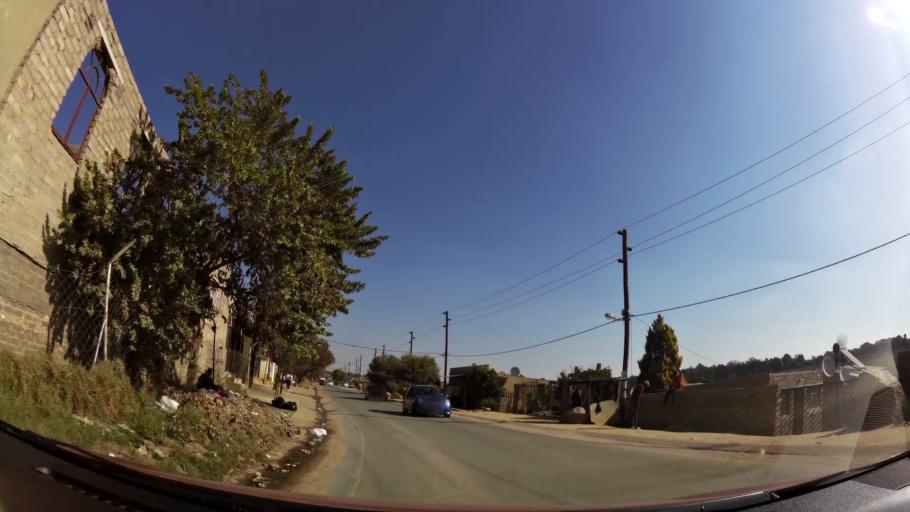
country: ZA
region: Gauteng
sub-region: West Rand District Municipality
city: Muldersdriseloop
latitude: -26.0184
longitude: 27.9228
